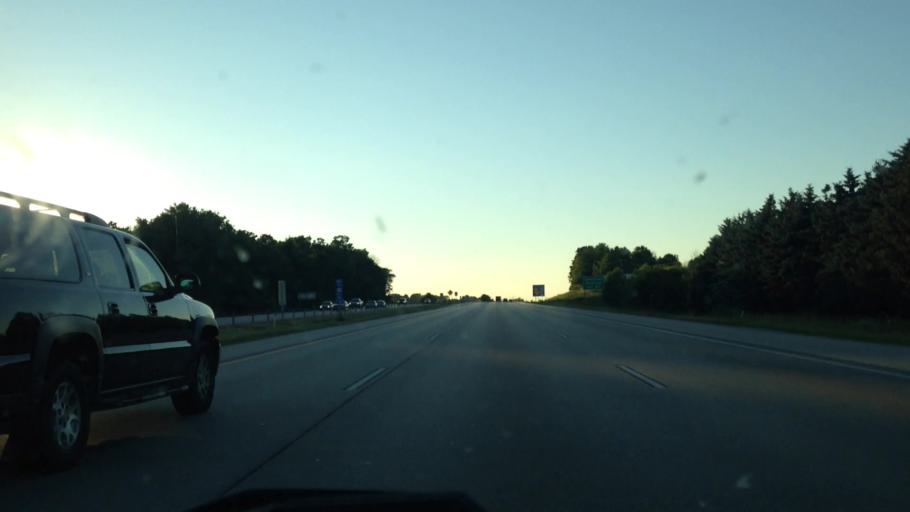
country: US
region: Wisconsin
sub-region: Washington County
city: Richfield
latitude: 43.2369
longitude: -88.1749
